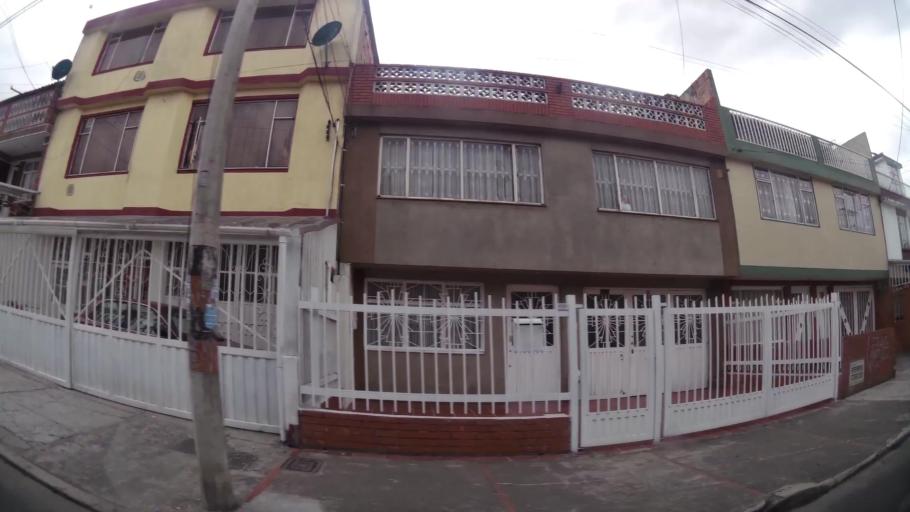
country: CO
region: Bogota D.C.
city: Barrio San Luis
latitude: 4.6961
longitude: -74.1015
